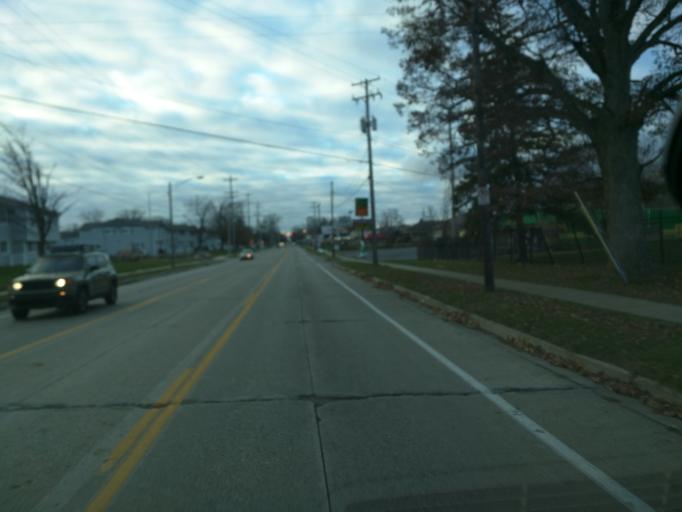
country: US
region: Michigan
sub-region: Eaton County
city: Waverly
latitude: 42.6858
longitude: -84.6031
